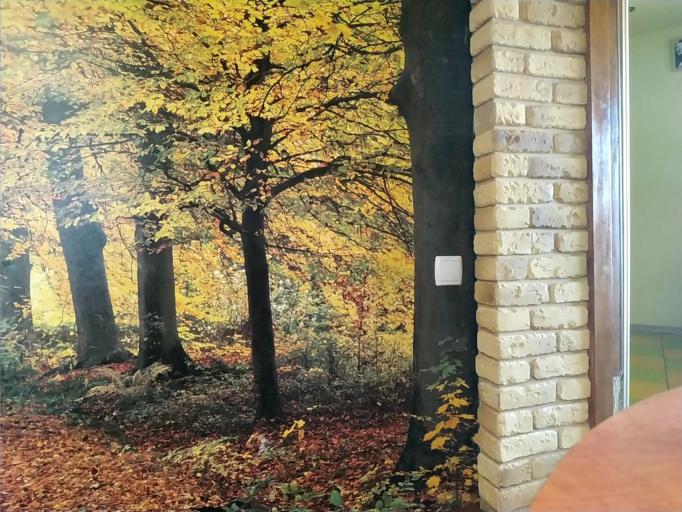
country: RU
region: Arkhangelskaya
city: Kargopol'
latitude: 60.7983
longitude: 38.8895
